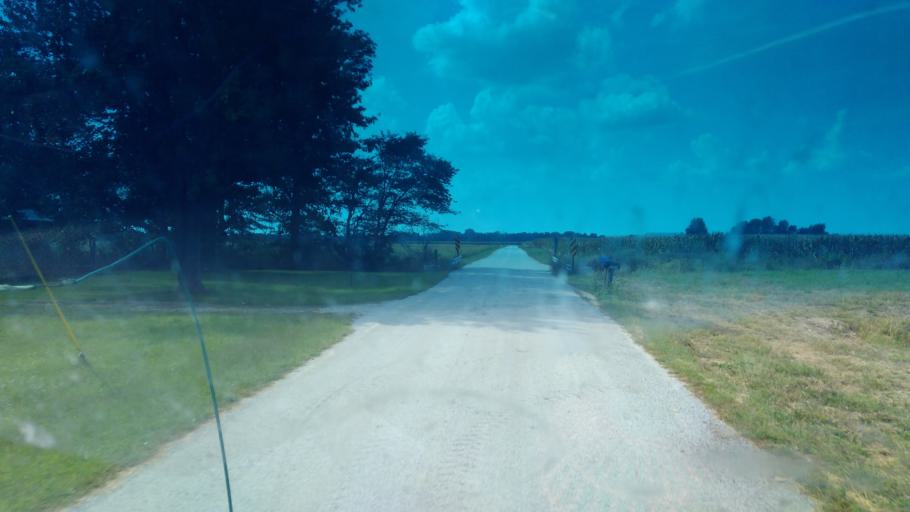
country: US
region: Ohio
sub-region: Hardin County
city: Kenton
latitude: 40.6894
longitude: -83.7252
